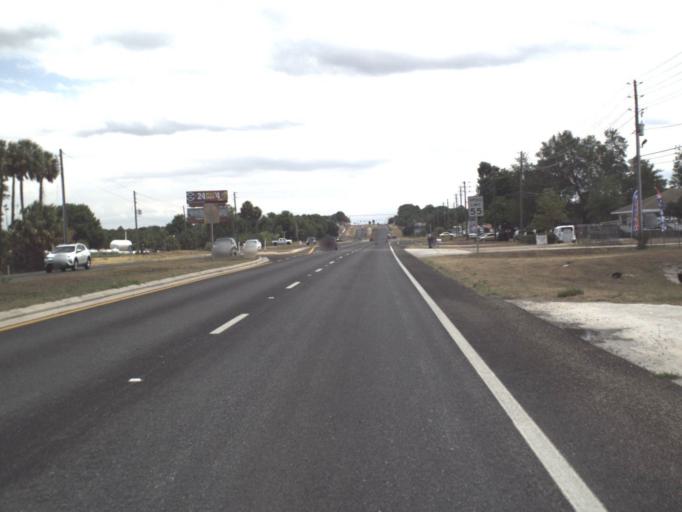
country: US
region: Florida
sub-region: Lake County
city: Groveland
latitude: 28.5580
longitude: -81.8339
